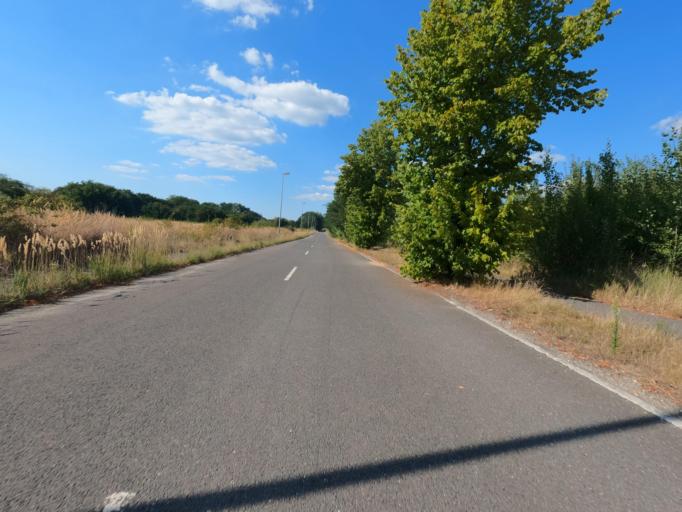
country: DE
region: North Rhine-Westphalia
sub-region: Regierungsbezirk Koln
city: Wassenberg
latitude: 51.0836
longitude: 6.1722
